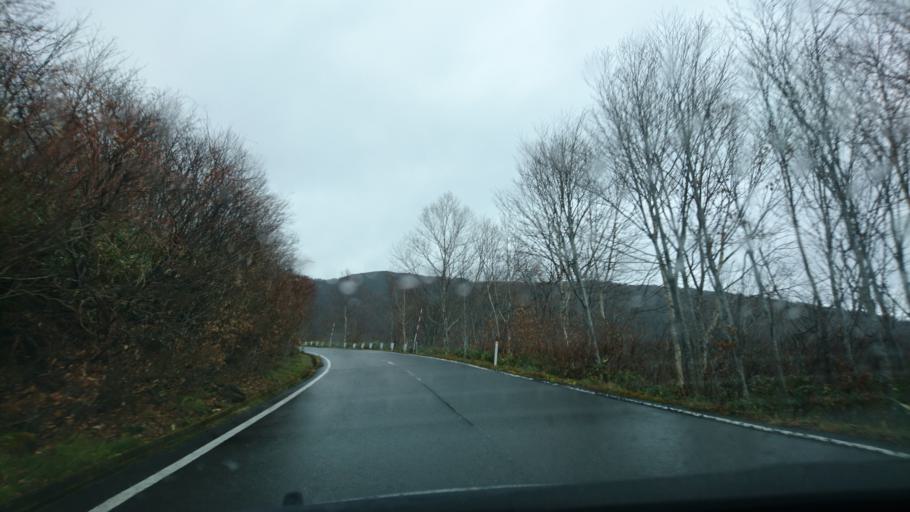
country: JP
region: Iwate
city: Ichinoseki
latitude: 38.9436
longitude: 140.8139
